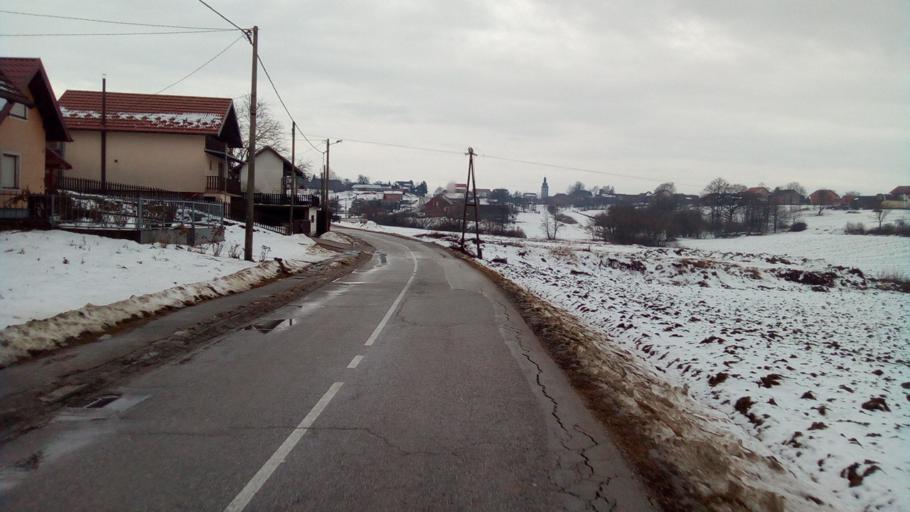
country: HR
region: Zagrebacka
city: Lupoglav
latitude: 45.7473
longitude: 16.4246
